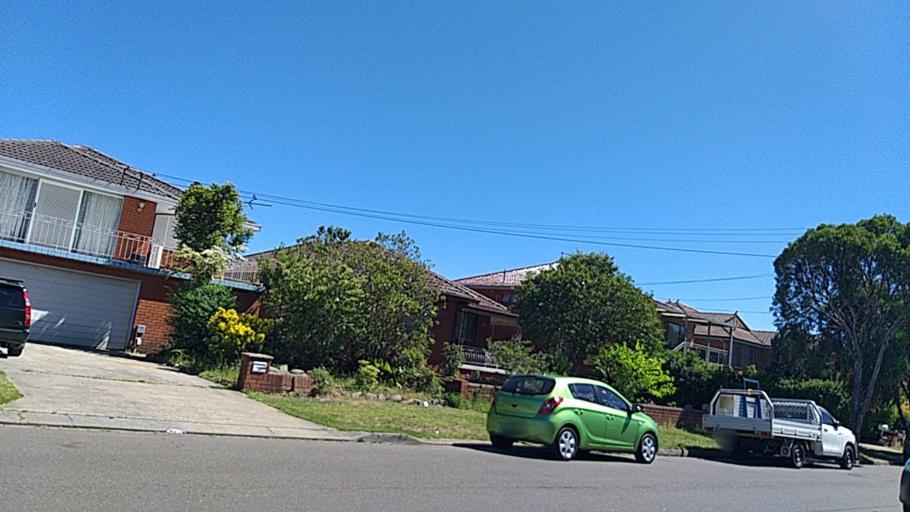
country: AU
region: New South Wales
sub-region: Fairfield
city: Cabramatta West
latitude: -33.9200
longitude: 150.9163
